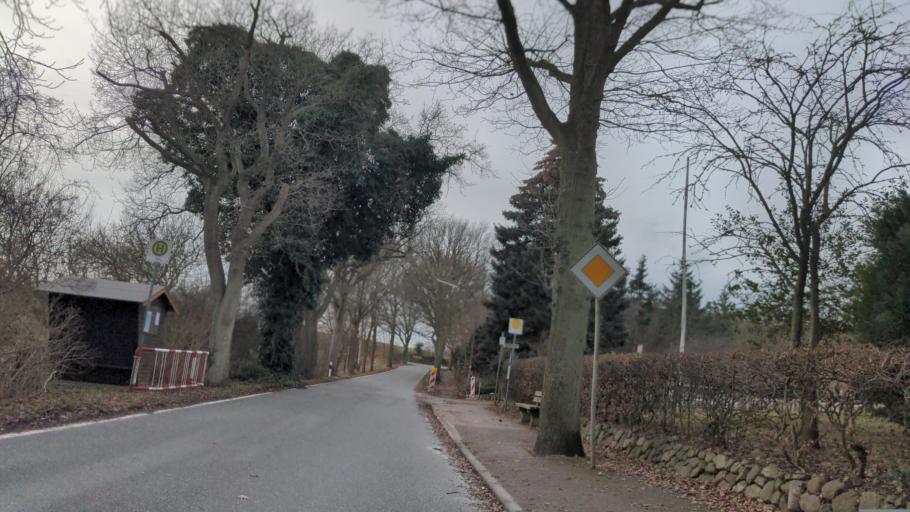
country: DE
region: Schleswig-Holstein
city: Neukirchen
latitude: 54.2047
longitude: 10.5861
